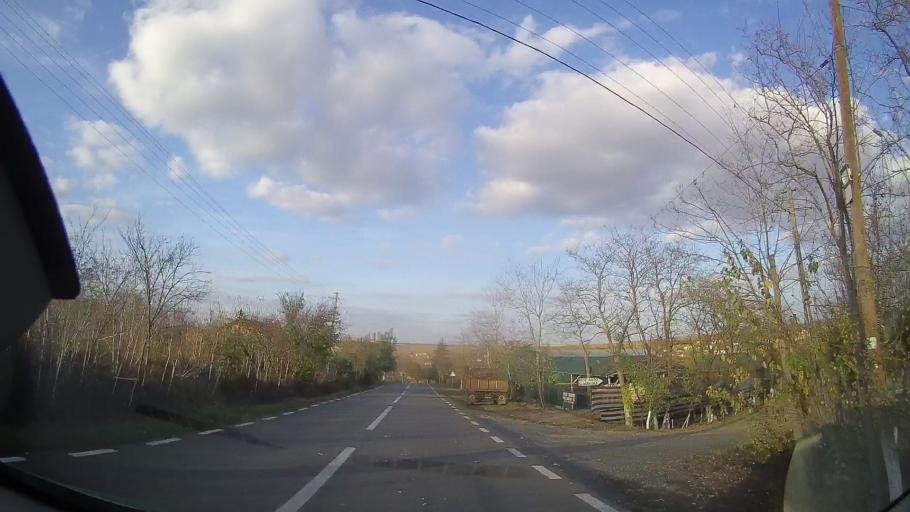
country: RO
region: Constanta
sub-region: Comuna Independenta
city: Independenta
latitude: 43.9524
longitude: 28.0751
